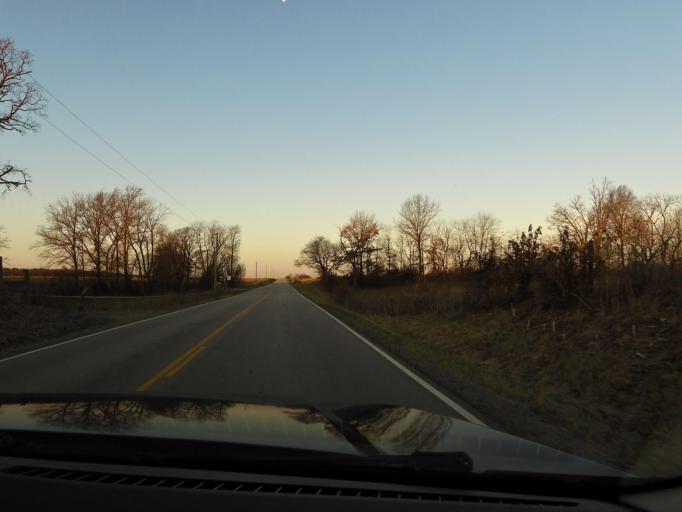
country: US
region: Illinois
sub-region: Marion County
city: Salem
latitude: 38.7588
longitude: -88.9047
